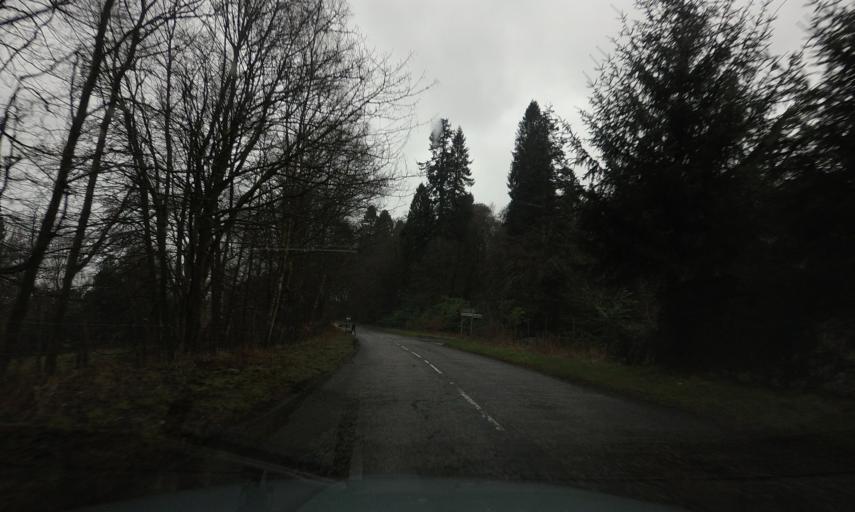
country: GB
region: Scotland
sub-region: Stirling
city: Balfron
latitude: 56.1569
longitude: -4.3643
